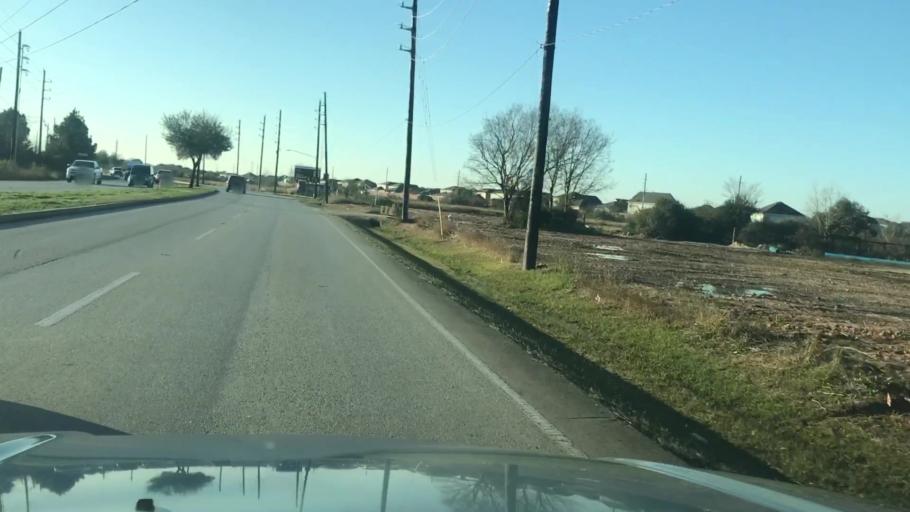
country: US
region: Texas
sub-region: Fort Bend County
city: Cinco Ranch
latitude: 29.8316
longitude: -95.7390
